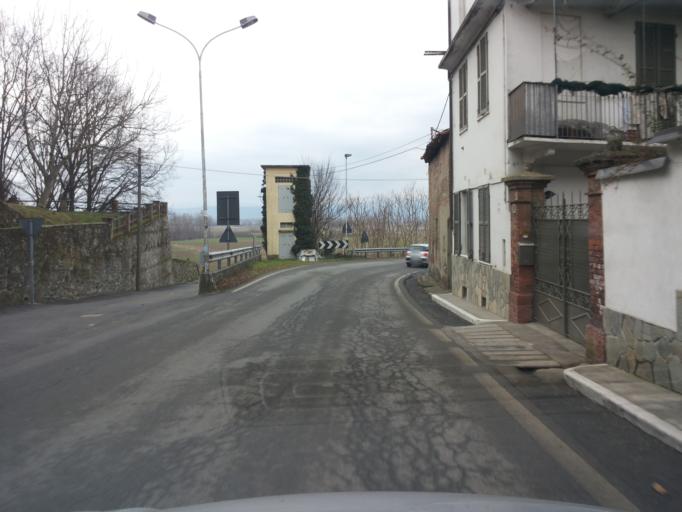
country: IT
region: Piedmont
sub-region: Provincia di Torino
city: Borgomasino
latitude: 45.3621
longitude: 7.9879
